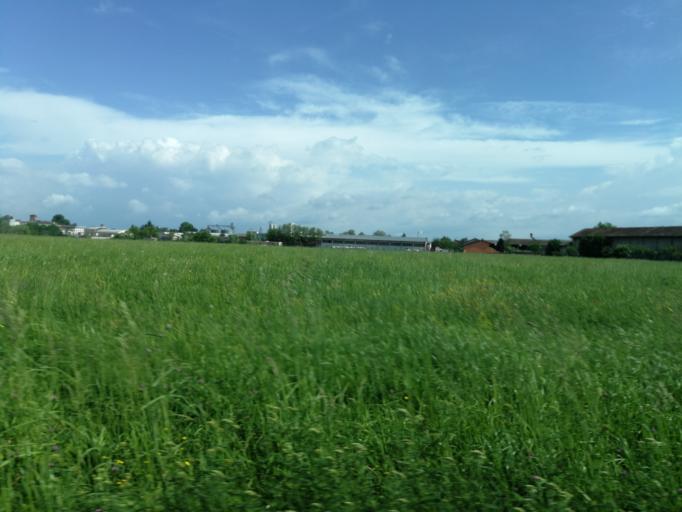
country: IT
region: Piedmont
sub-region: Provincia di Cuneo
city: Faule
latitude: 44.8087
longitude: 7.5825
